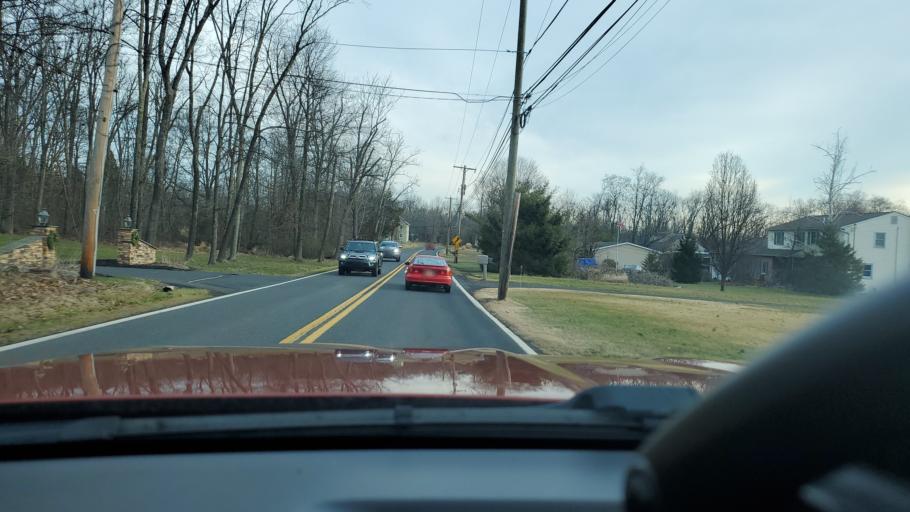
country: US
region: Pennsylvania
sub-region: Montgomery County
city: Woxall
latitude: 40.3290
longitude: -75.4146
